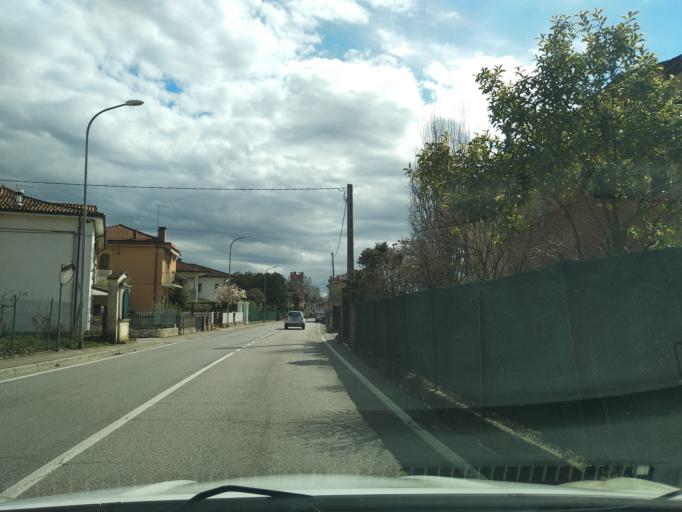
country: IT
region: Veneto
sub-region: Provincia di Vicenza
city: Monticello Conte Otto
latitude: 45.5965
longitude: 11.5784
